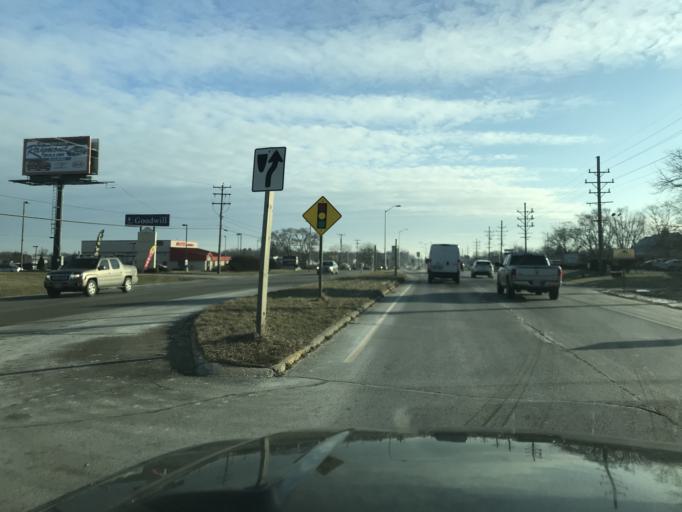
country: US
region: Wisconsin
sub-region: Kenosha County
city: Pleasant Prairie
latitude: 42.5666
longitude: -87.8832
